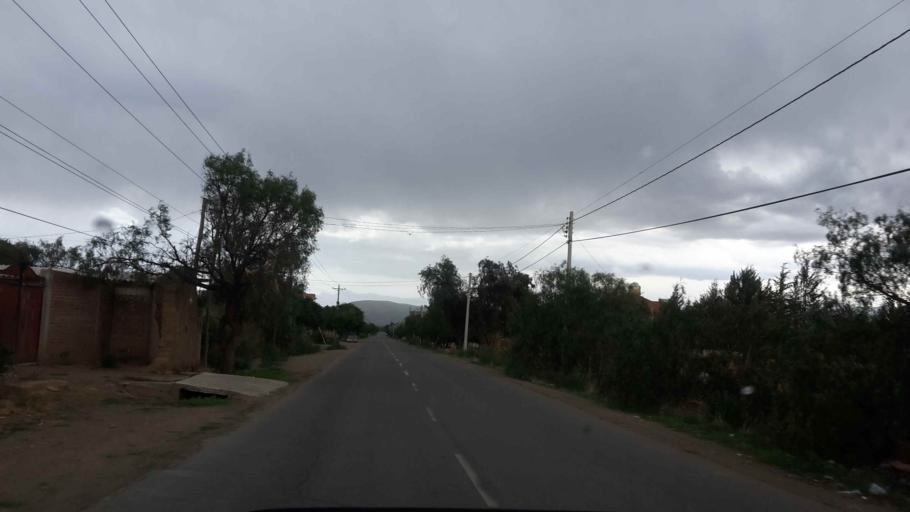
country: BO
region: Cochabamba
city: Tarata
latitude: -17.5897
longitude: -66.0468
